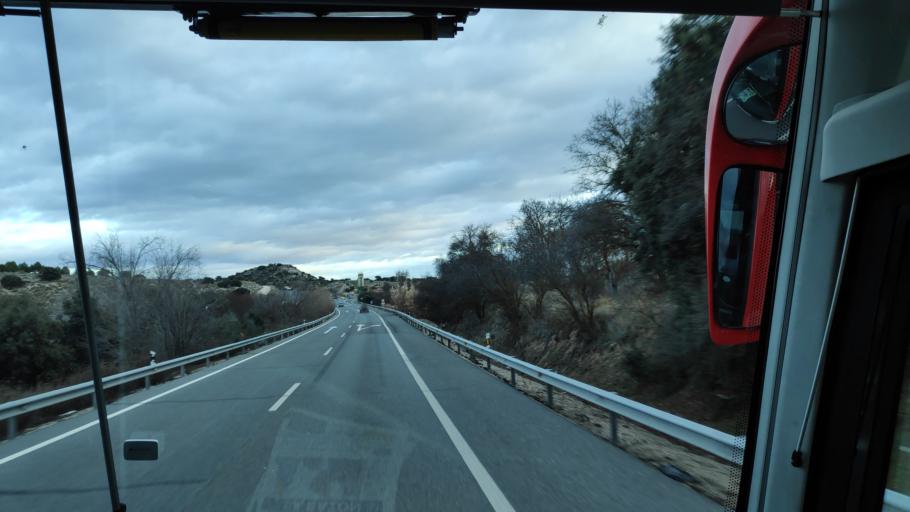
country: ES
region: Madrid
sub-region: Provincia de Madrid
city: Villarejo de Salvanes
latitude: 40.1461
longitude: -3.2169
